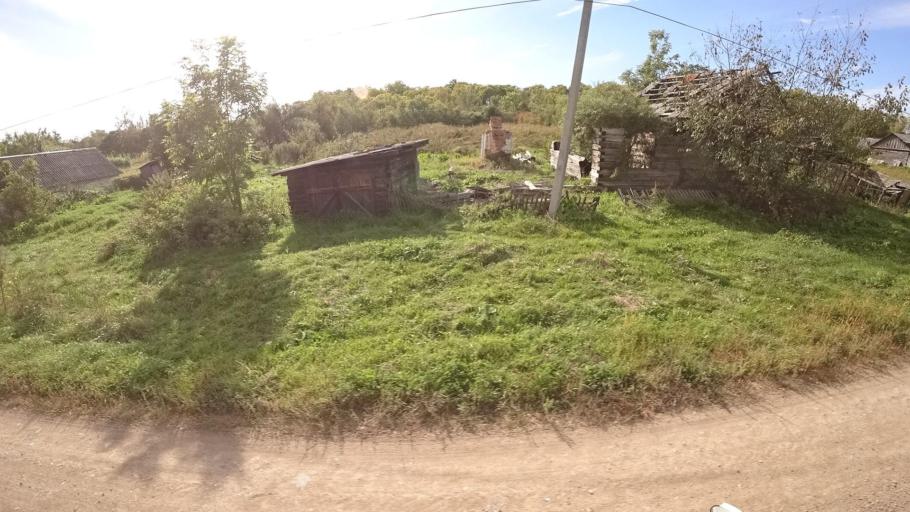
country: RU
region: Primorskiy
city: Dostoyevka
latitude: 44.2984
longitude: 133.4600
